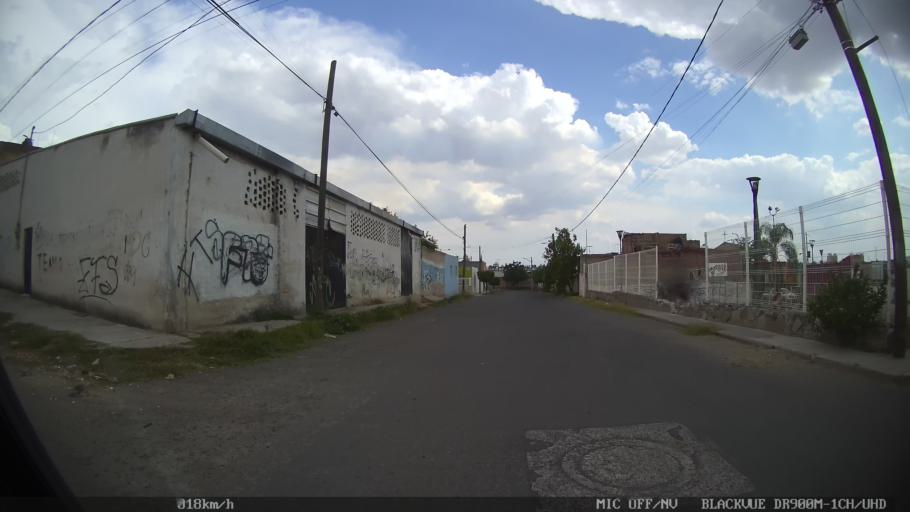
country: MX
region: Jalisco
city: Tlaquepaque
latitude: 20.6289
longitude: -103.2788
